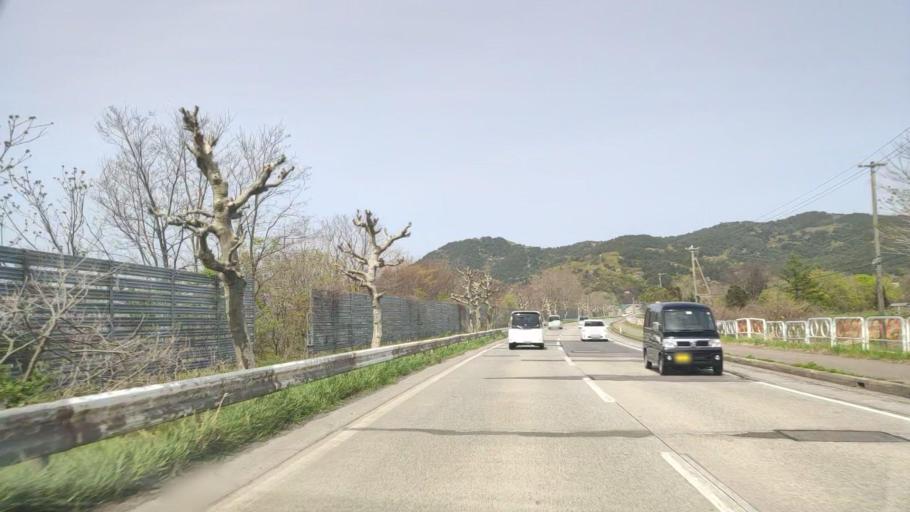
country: JP
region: Aomori
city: Aomori Shi
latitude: 40.8669
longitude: 140.8465
